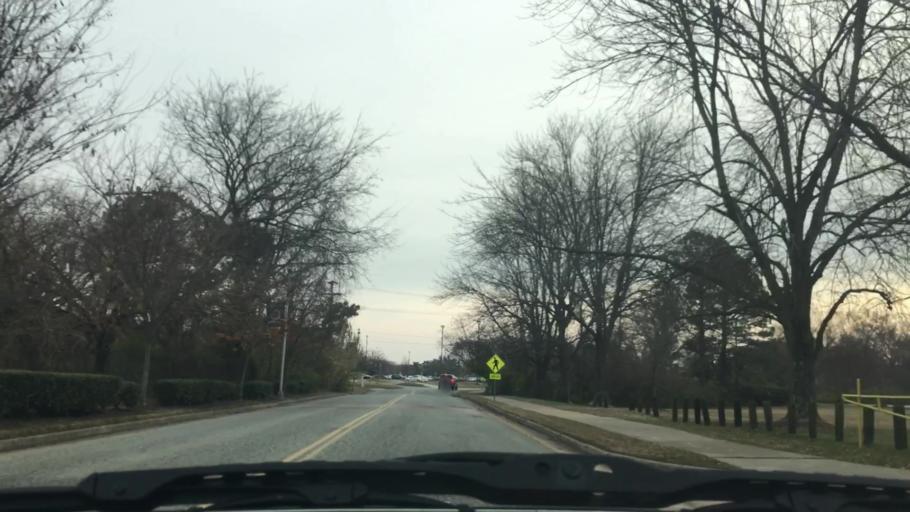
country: US
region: Virginia
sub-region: City of Hampton
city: East Hampton
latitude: 37.0206
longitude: -76.3301
